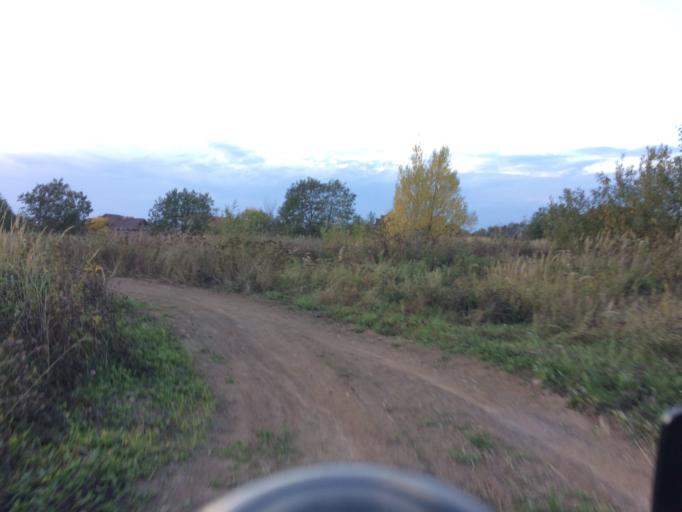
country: RU
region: Mariy-El
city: Yoshkar-Ola
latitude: 56.6472
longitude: 47.9212
